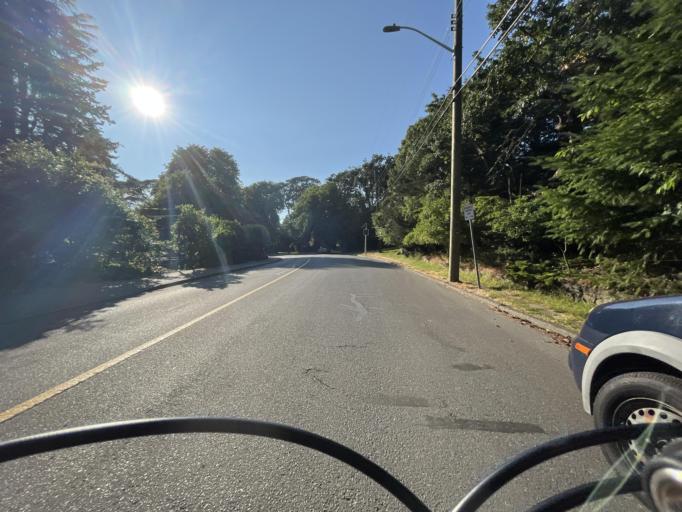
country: CA
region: British Columbia
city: Victoria
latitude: 48.4204
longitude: -123.3458
